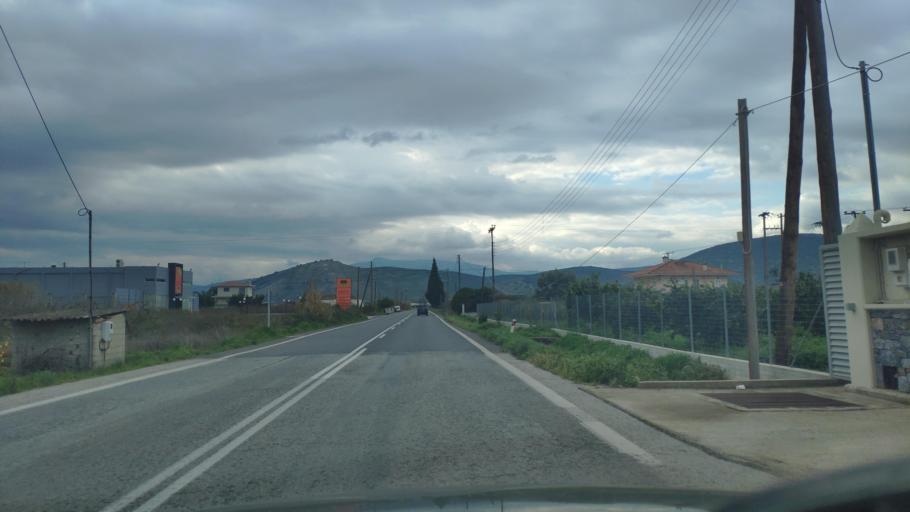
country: GR
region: Peloponnese
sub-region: Nomos Argolidos
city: Nea Kios
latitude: 37.5772
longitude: 22.7087
